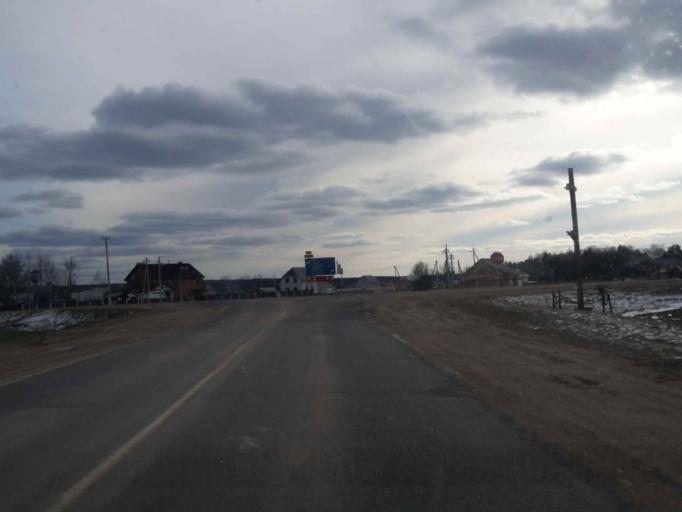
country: BY
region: Minsk
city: Il'ya
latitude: 54.5114
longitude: 27.2212
